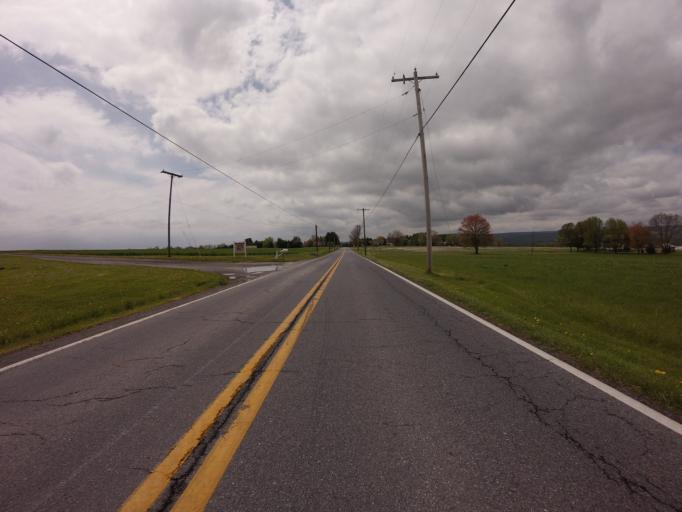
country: US
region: Maryland
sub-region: Frederick County
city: Walkersville
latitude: 39.5428
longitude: -77.3795
